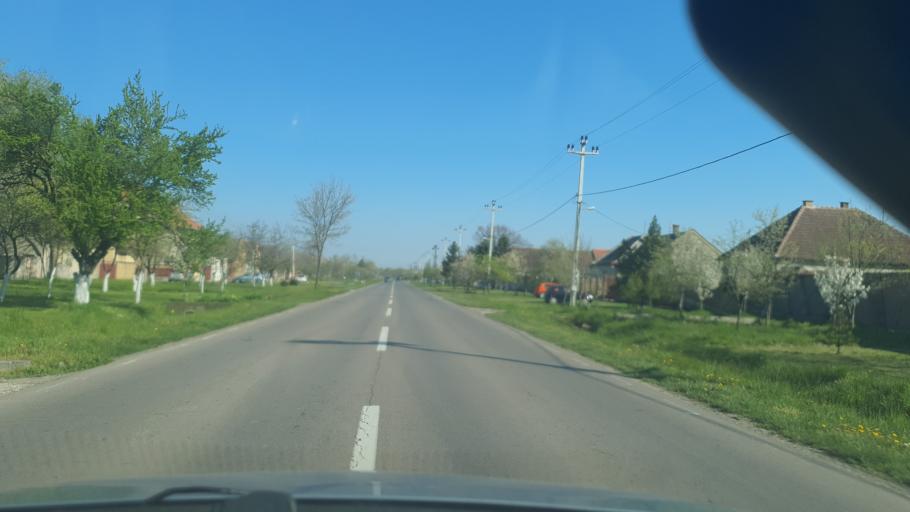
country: RS
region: Autonomna Pokrajina Vojvodina
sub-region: Zapadnobacki Okrug
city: Kula
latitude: 45.7143
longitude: 19.3785
